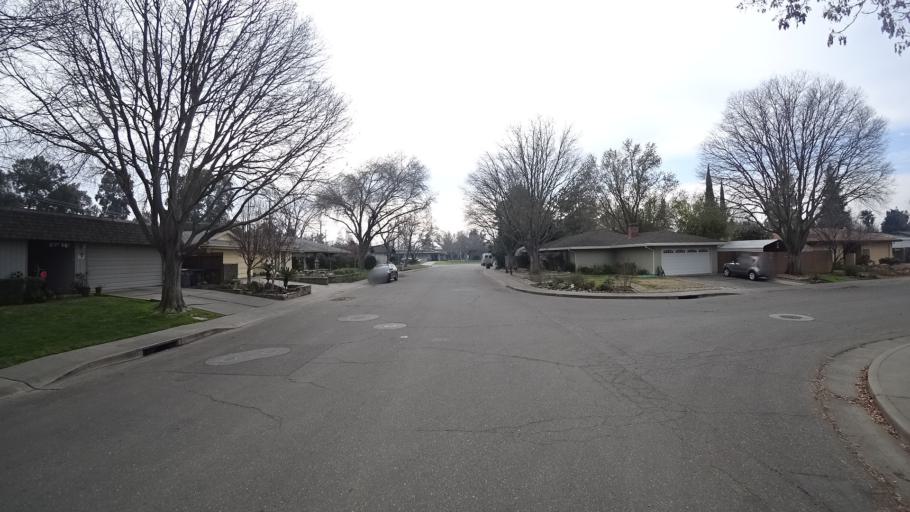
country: US
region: California
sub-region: Yolo County
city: Davis
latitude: 38.5582
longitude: -121.7363
